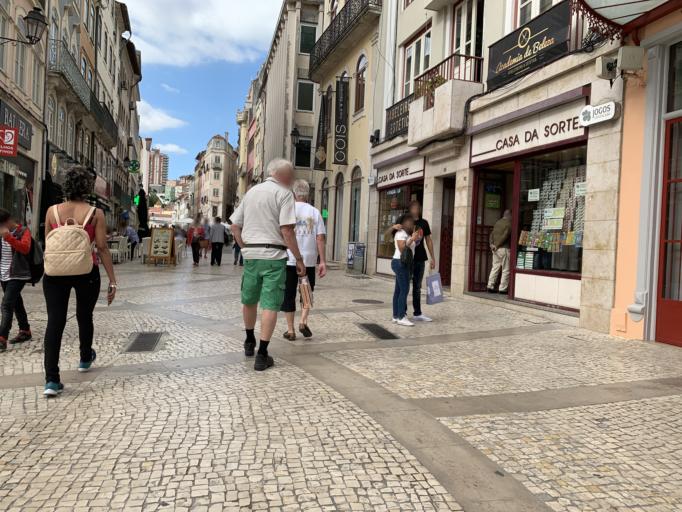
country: PT
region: Coimbra
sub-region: Coimbra
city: Coimbra
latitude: 40.2087
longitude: -8.4291
